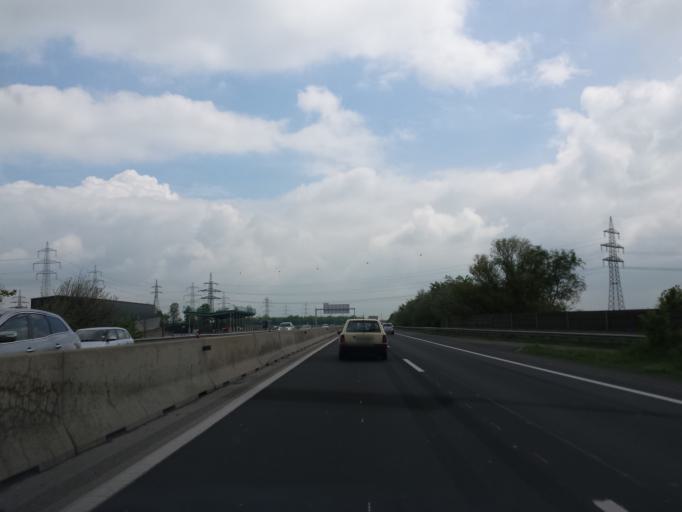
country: AT
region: Burgenland
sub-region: Politischer Bezirk Neusiedl am See
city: Bruckneudorf
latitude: 48.0430
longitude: 16.7751
